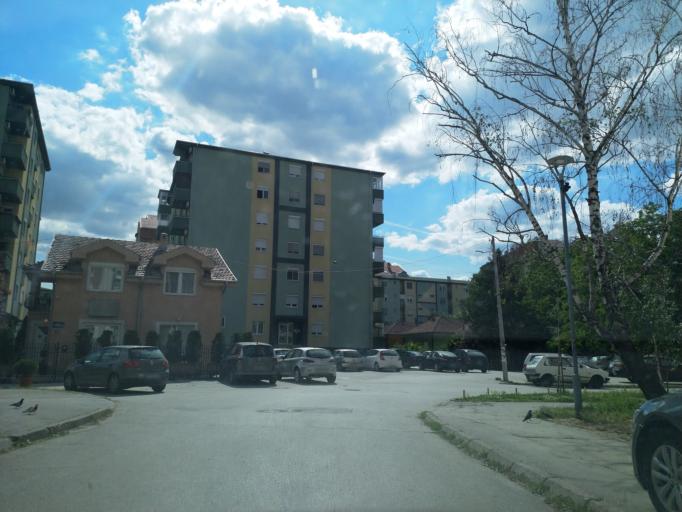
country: RS
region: Central Serbia
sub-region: Pomoravski Okrug
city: Jagodina
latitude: 43.9784
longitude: 21.2656
